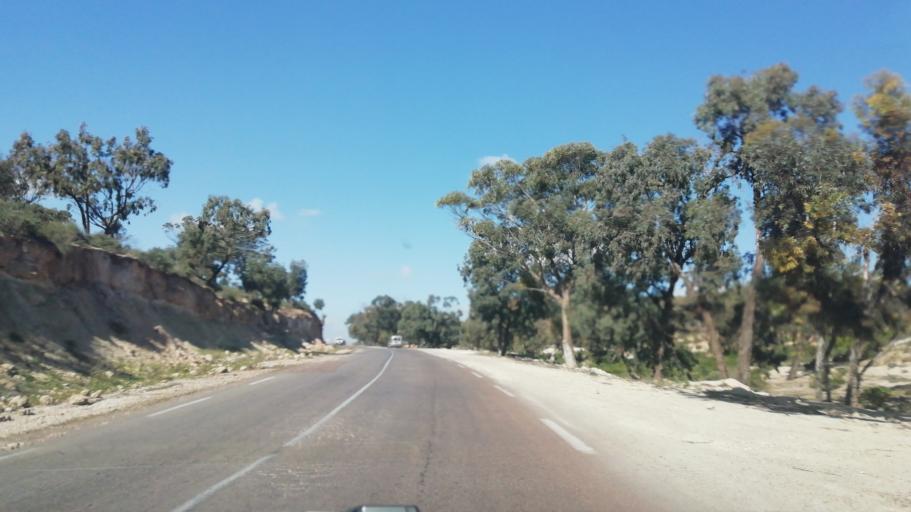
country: DZ
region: Oran
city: Ain el Bya
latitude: 35.7136
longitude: -0.2270
